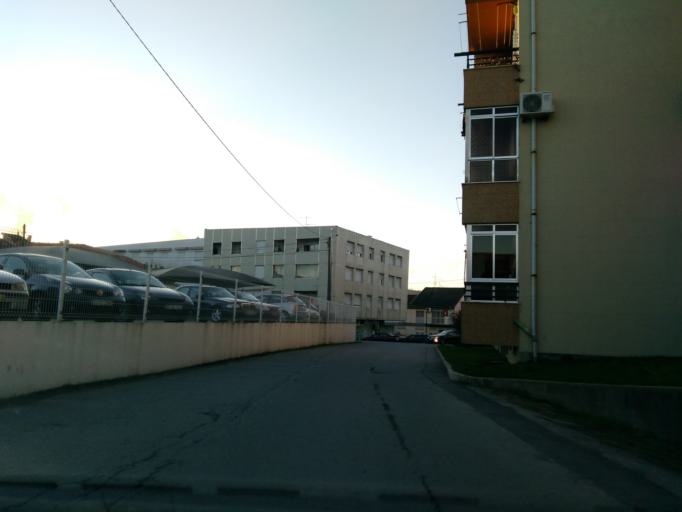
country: PT
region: Braga
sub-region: Braga
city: Braga
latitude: 41.5376
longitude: -8.4389
